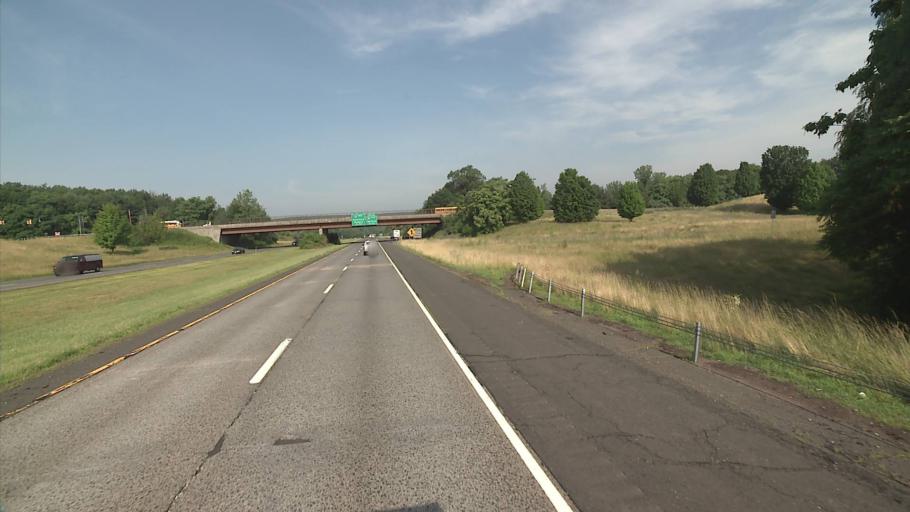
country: US
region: Connecticut
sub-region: New Haven County
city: Cheshire Village
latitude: 41.5569
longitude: -72.8888
